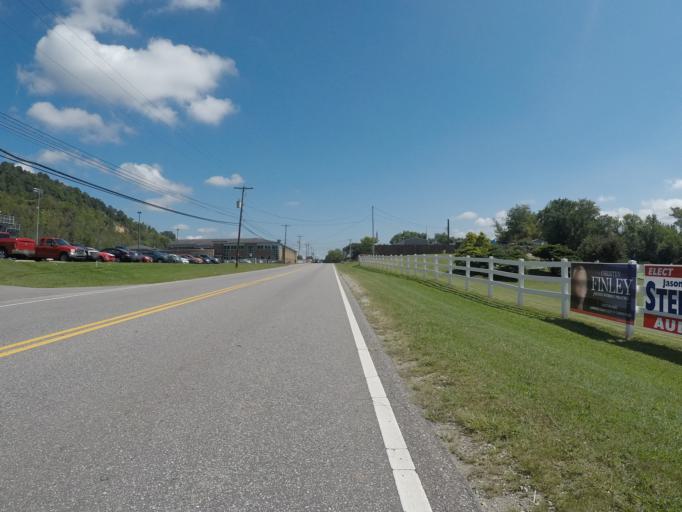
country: US
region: West Virginia
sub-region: Cabell County
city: Huntington
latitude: 38.4222
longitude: -82.4853
